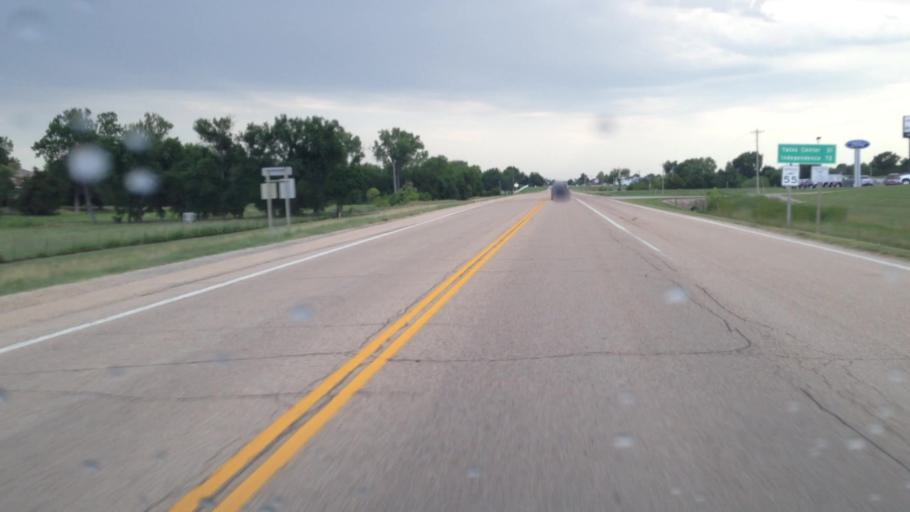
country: US
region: Kansas
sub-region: Coffey County
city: Burlington
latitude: 38.1860
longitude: -95.7387
